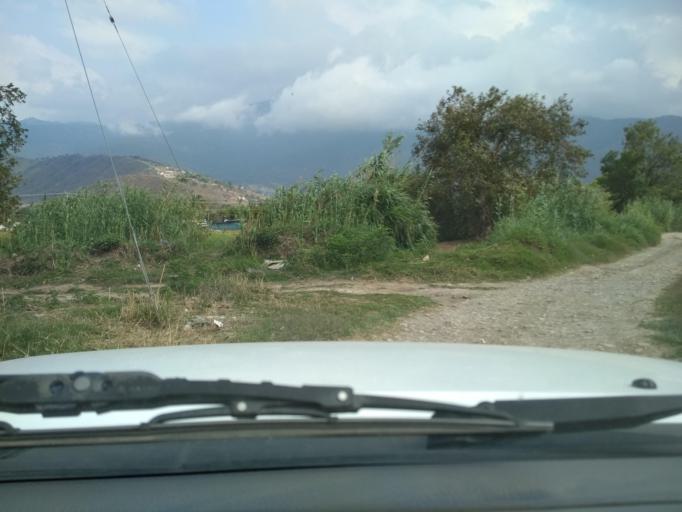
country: MX
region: Veracruz
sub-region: Acultzingo
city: Acatla
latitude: 18.7697
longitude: -97.2247
